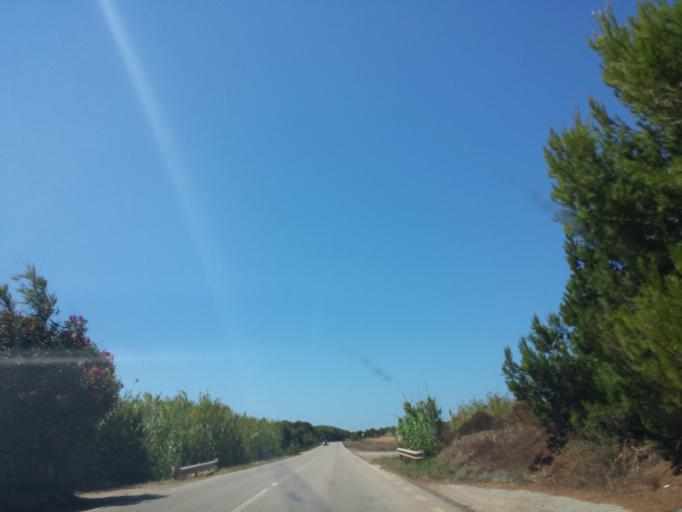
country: IT
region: Sardinia
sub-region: Provincia di Carbonia-Iglesias
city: Gonnesa
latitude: 39.2835
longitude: 8.4475
